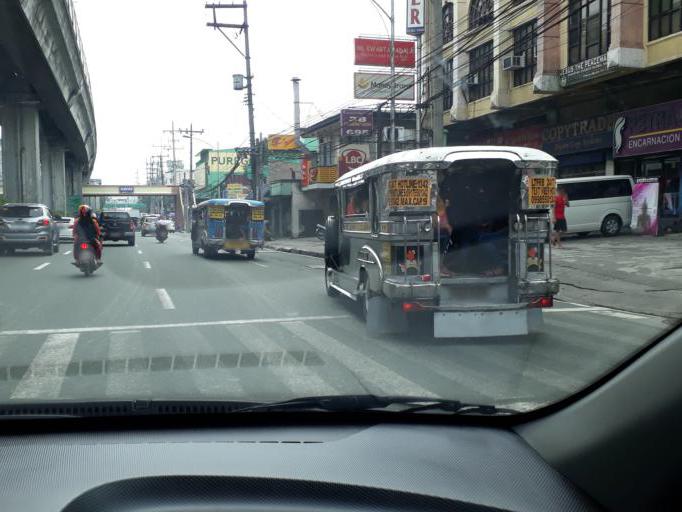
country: PH
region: Metro Manila
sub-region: City of Manila
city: Quiapo
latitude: 14.6017
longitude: 121.0044
